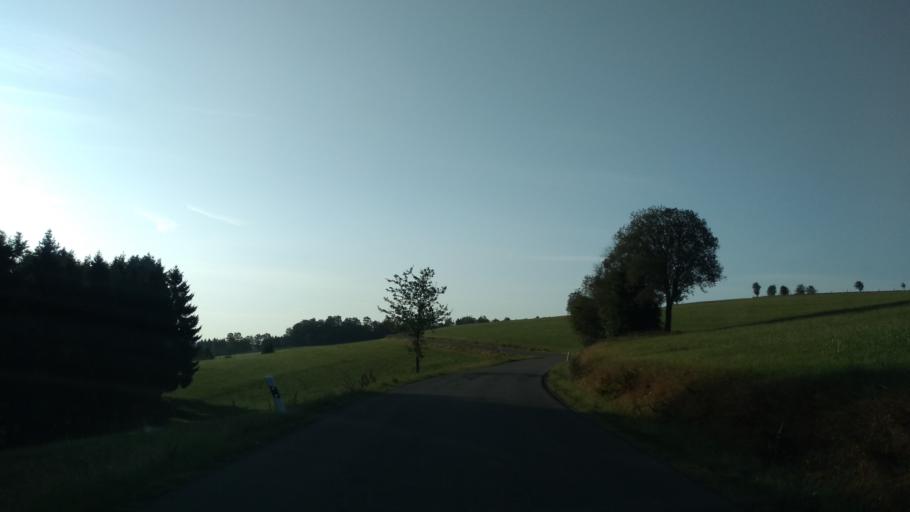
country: DE
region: North Rhine-Westphalia
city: Kierspe
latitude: 51.0807
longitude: 7.5950
